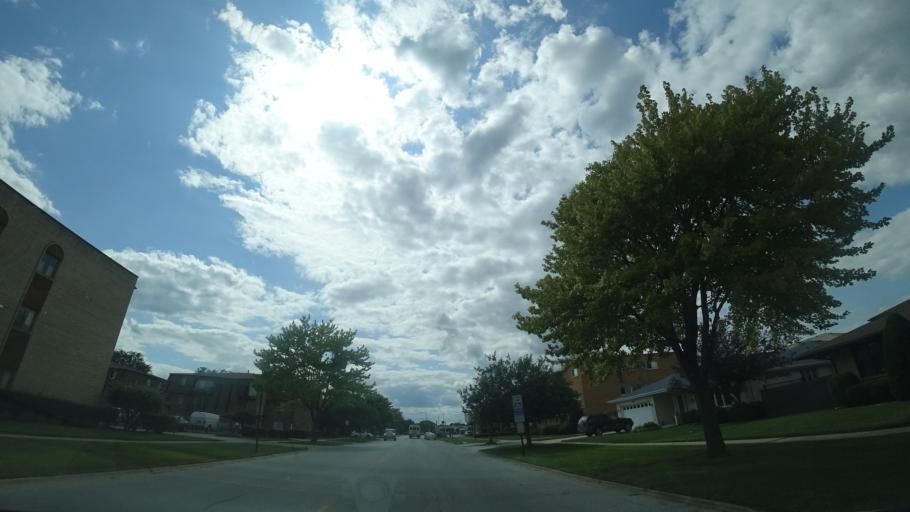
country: US
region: Illinois
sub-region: Cook County
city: Oak Lawn
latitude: 41.6983
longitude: -87.7376
